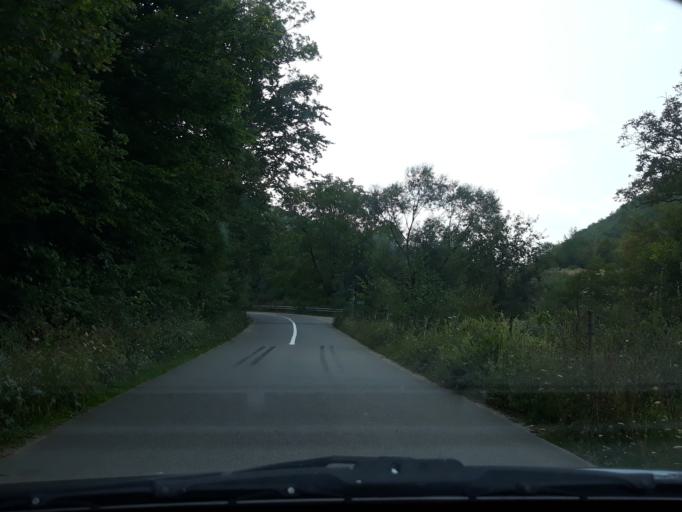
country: RO
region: Bihor
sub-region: Comuna Pietroasa
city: Pietroasa
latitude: 46.5896
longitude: 22.5820
